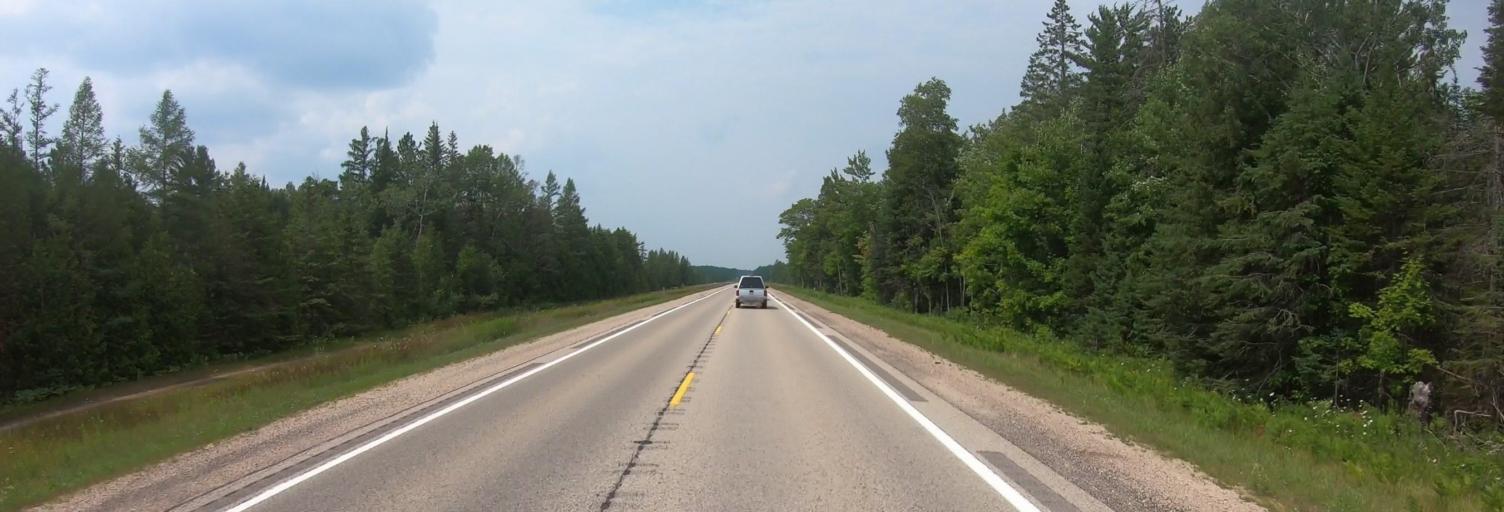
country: US
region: Michigan
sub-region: Alger County
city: Munising
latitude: 46.3761
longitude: -86.5605
